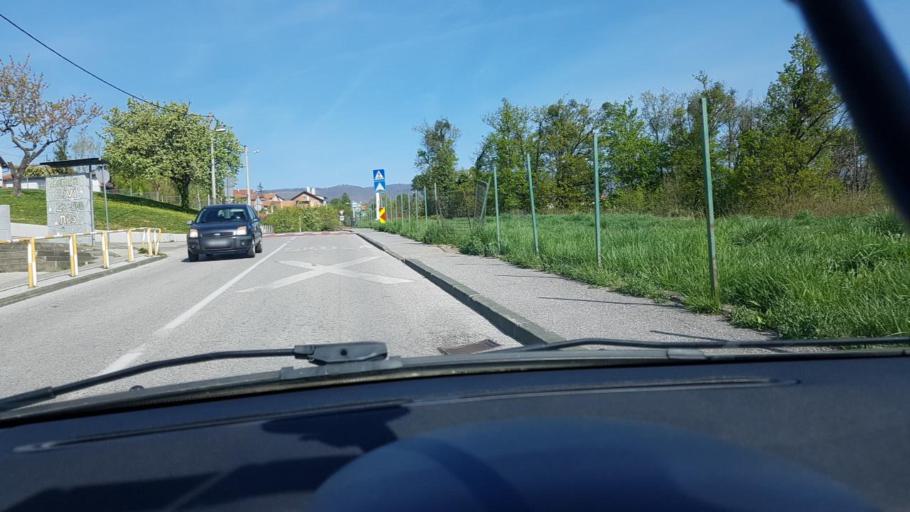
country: HR
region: Grad Zagreb
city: Zagreb
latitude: 45.8481
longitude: 15.9915
